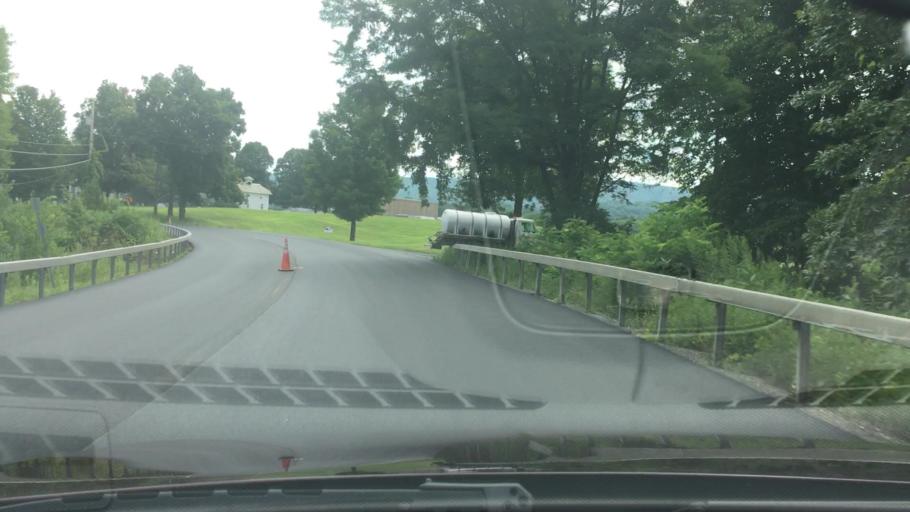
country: US
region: New York
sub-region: Dutchess County
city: Hillside Lake
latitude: 41.5779
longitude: -73.7384
